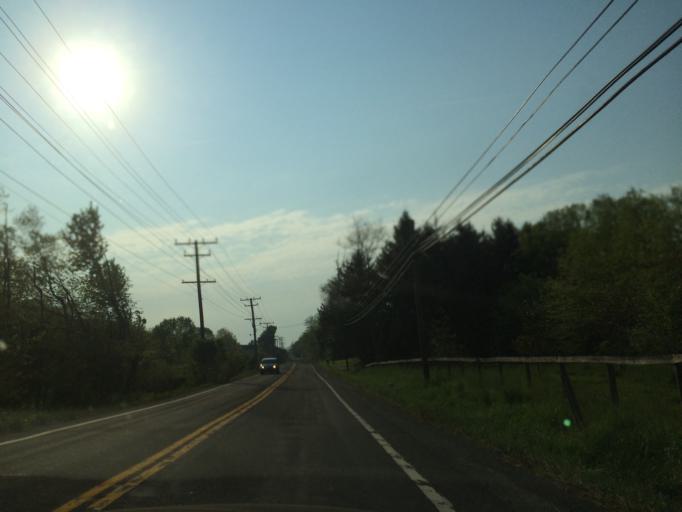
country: US
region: Maryland
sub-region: Carroll County
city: Sykesville
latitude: 39.3121
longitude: -76.9882
